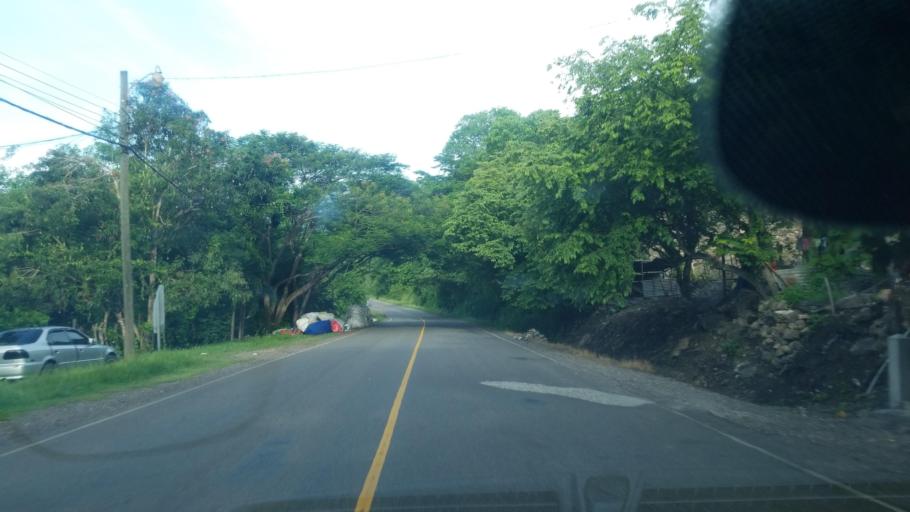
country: HN
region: Santa Barbara
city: Trinidad
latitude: 15.1224
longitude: -88.2051
